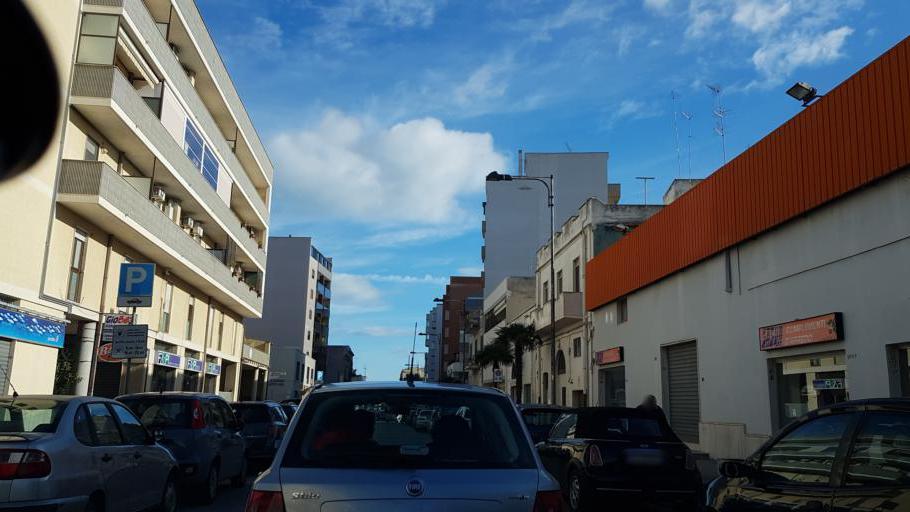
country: IT
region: Apulia
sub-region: Provincia di Brindisi
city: Brindisi
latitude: 40.6313
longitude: 17.9290
